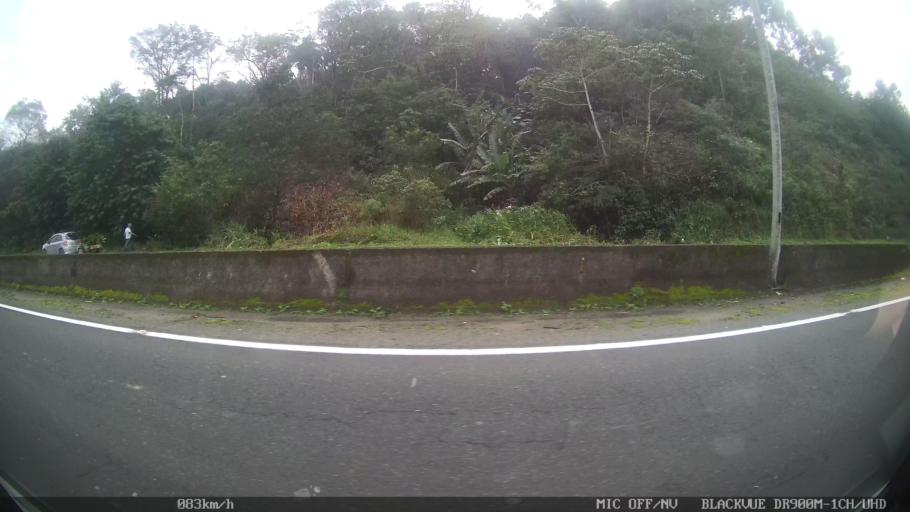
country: BR
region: Santa Catarina
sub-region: Penha
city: Penha
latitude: -26.8083
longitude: -48.6744
